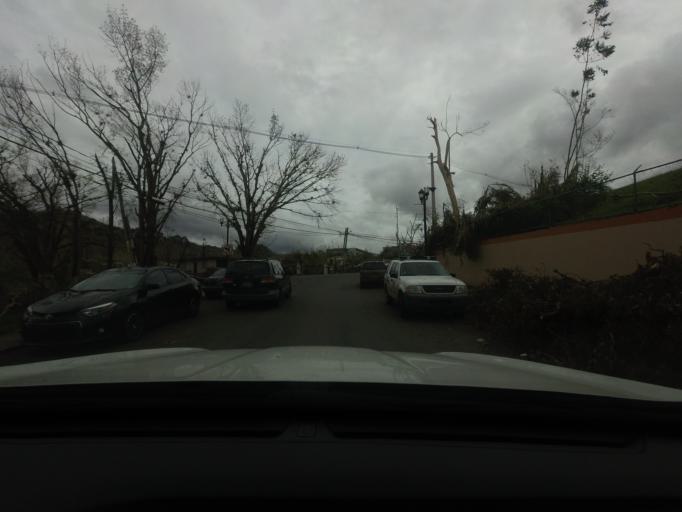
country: PR
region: Ciales
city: Ciales
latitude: 18.3417
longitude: -66.4685
